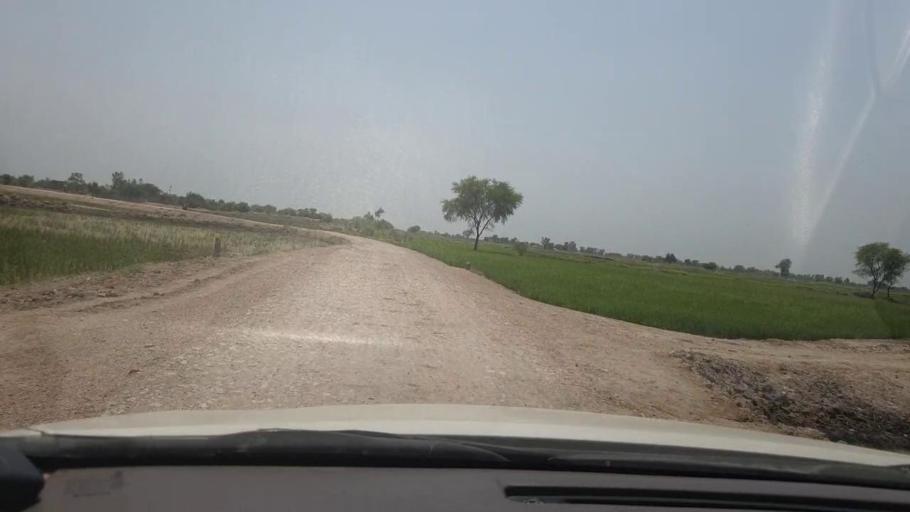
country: PK
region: Sindh
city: Garhi Yasin
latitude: 27.9226
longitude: 68.5514
